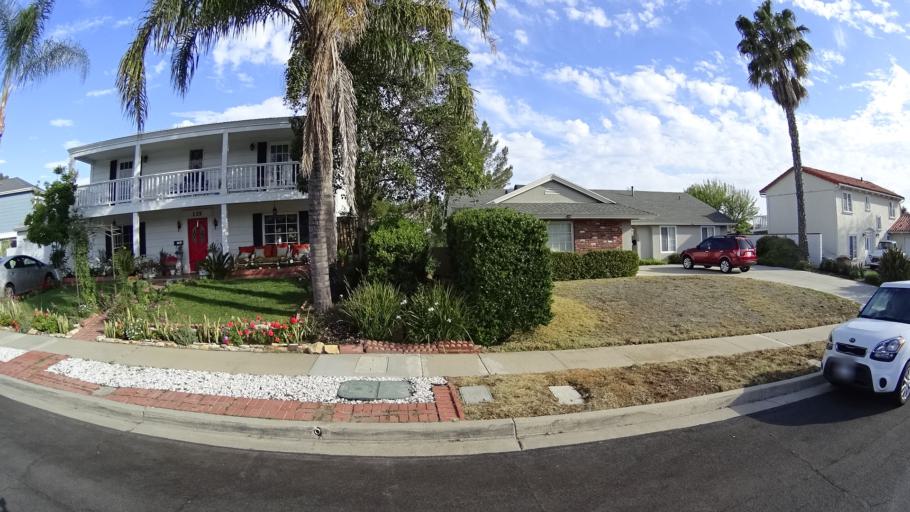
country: US
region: California
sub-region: Ventura County
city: Casa Conejo
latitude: 34.1777
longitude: -118.9500
